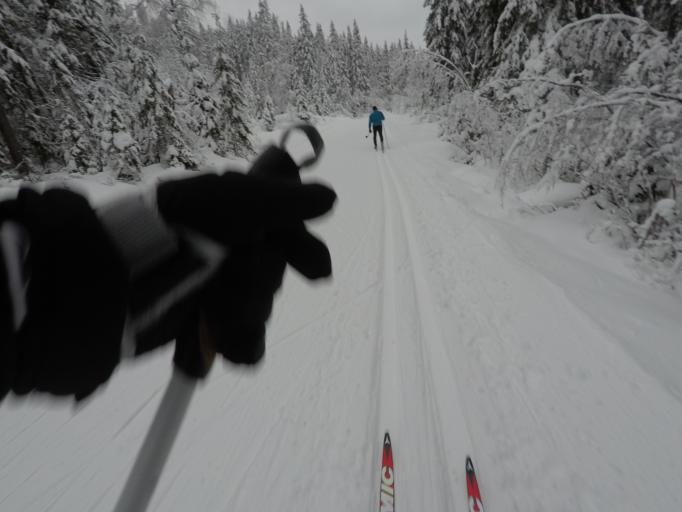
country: SE
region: Dalarna
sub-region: Ludvika Kommun
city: Abborrberget
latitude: 60.1480
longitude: 14.4843
